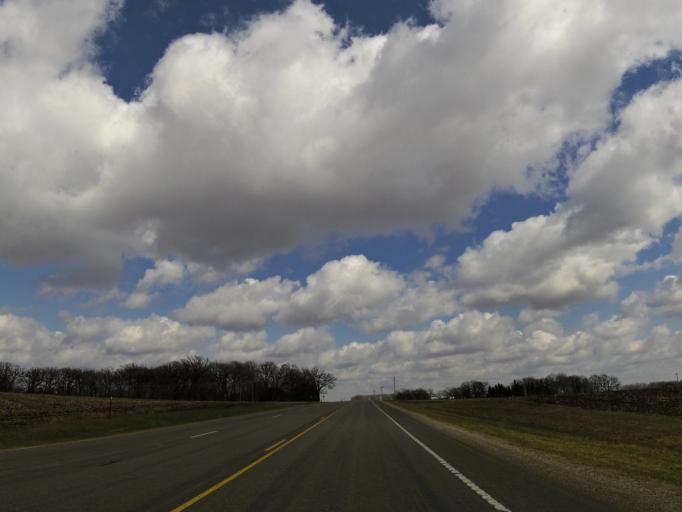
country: US
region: Minnesota
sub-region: Dodge County
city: Mantorville
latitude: 44.0801
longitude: -92.7512
